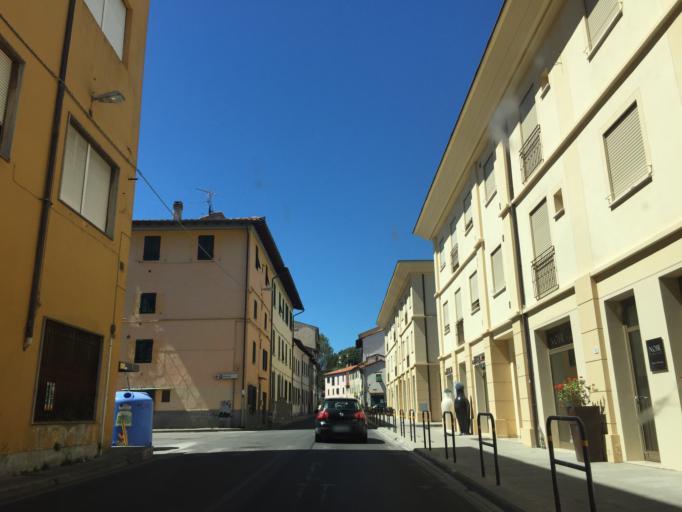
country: IT
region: Tuscany
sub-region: Provincia di Pistoia
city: Pistoia
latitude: 43.9296
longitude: 10.9104
